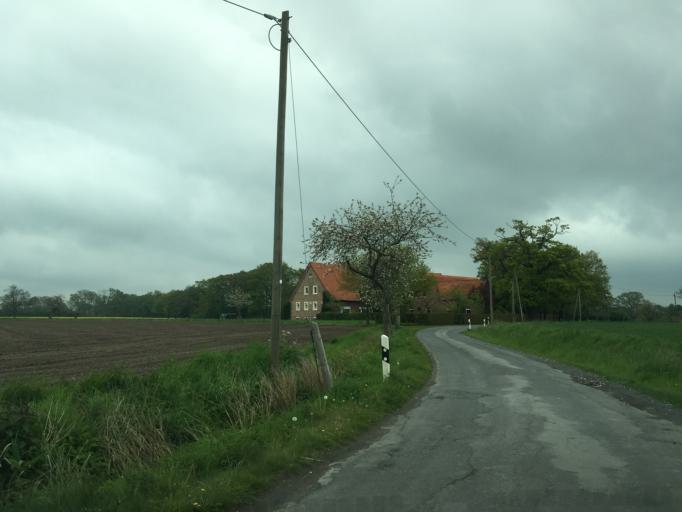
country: DE
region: North Rhine-Westphalia
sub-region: Regierungsbezirk Munster
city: Nordwalde
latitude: 52.0794
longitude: 7.4955
